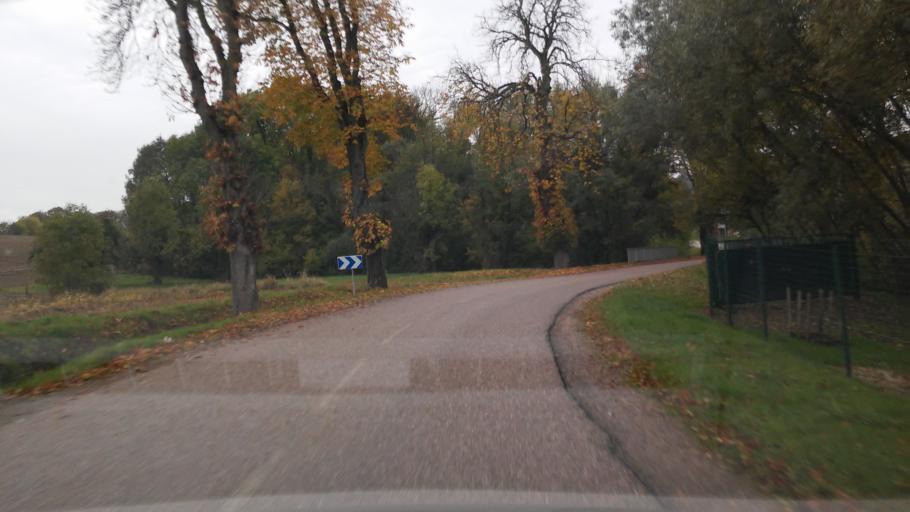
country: FR
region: Lorraine
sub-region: Departement de la Moselle
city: Boulay-Moselle
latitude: 49.1916
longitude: 6.4173
